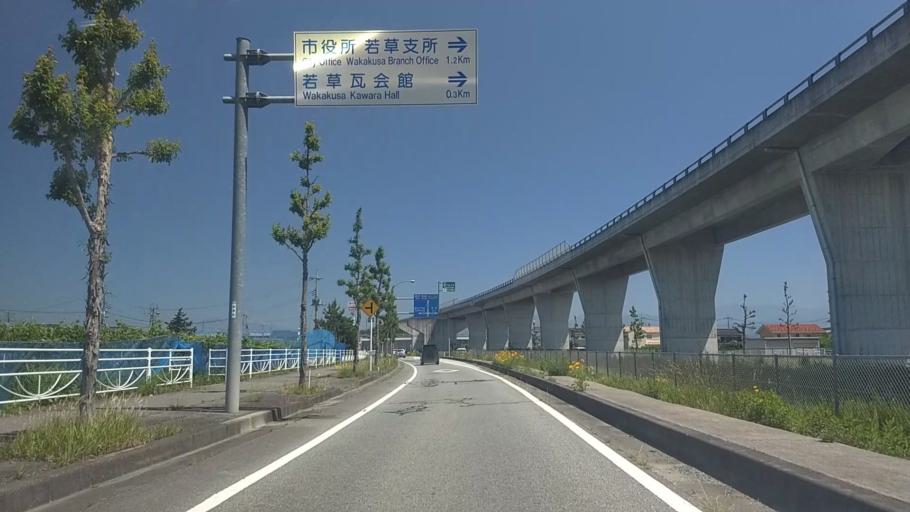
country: JP
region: Yamanashi
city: Ryuo
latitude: 35.6066
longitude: 138.4813
